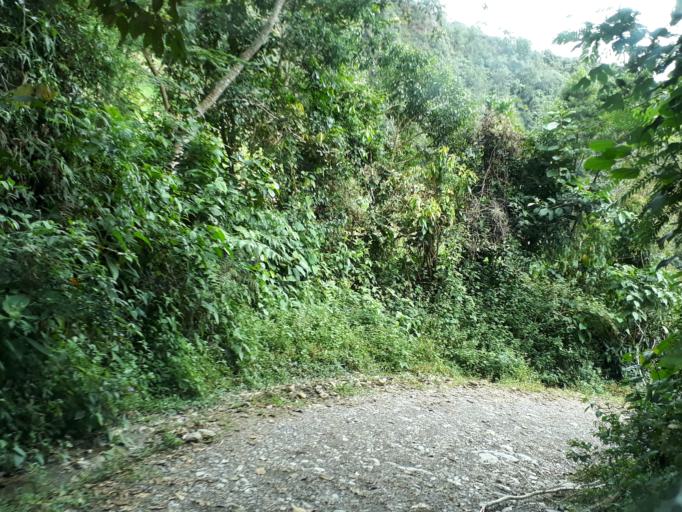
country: CO
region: Boyaca
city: Quipama
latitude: 5.3937
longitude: -74.1203
